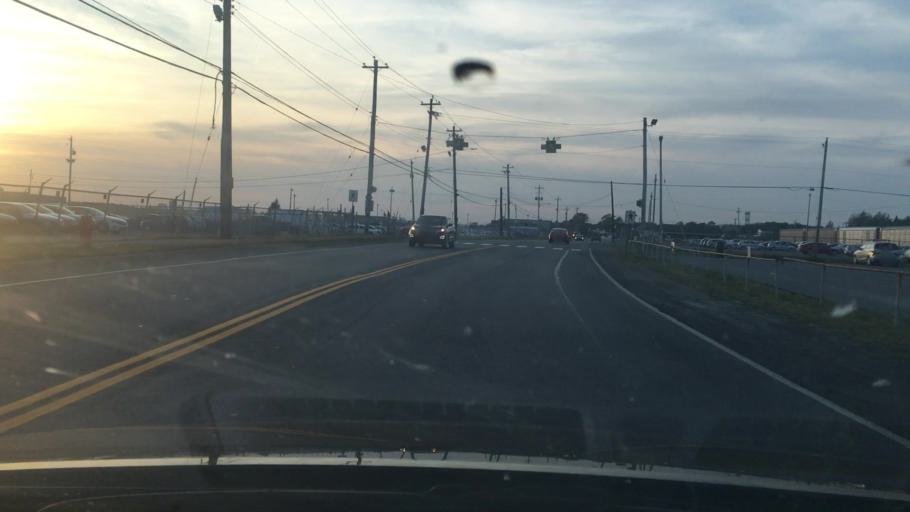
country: CA
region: Nova Scotia
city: Cole Harbour
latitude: 44.6207
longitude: -63.5066
